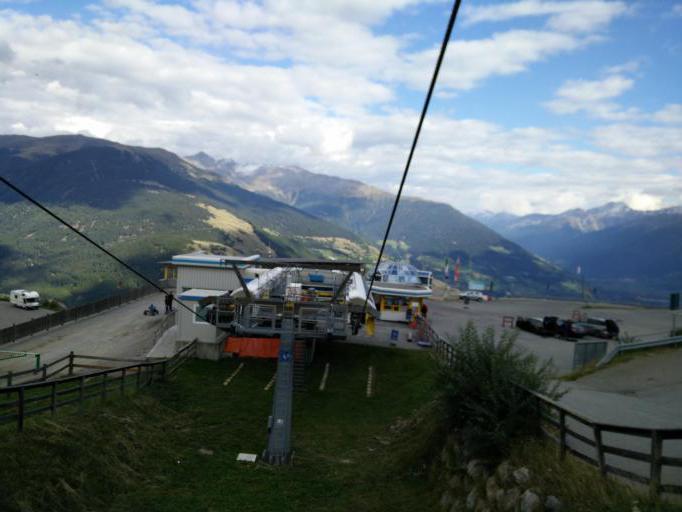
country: IT
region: Trentino-Alto Adige
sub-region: Bolzano
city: Malles Venosta
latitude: 46.7043
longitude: 10.5082
